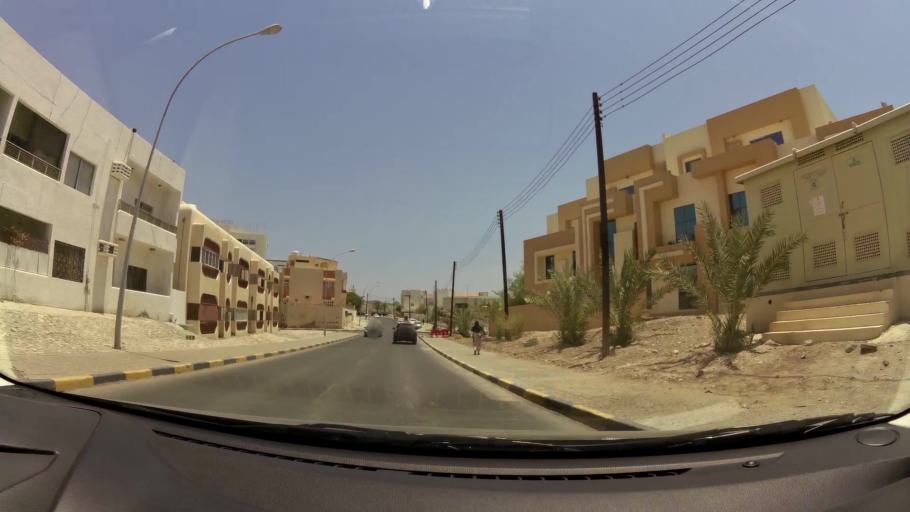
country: OM
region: Muhafazat Masqat
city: Muscat
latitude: 23.6044
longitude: 58.5388
